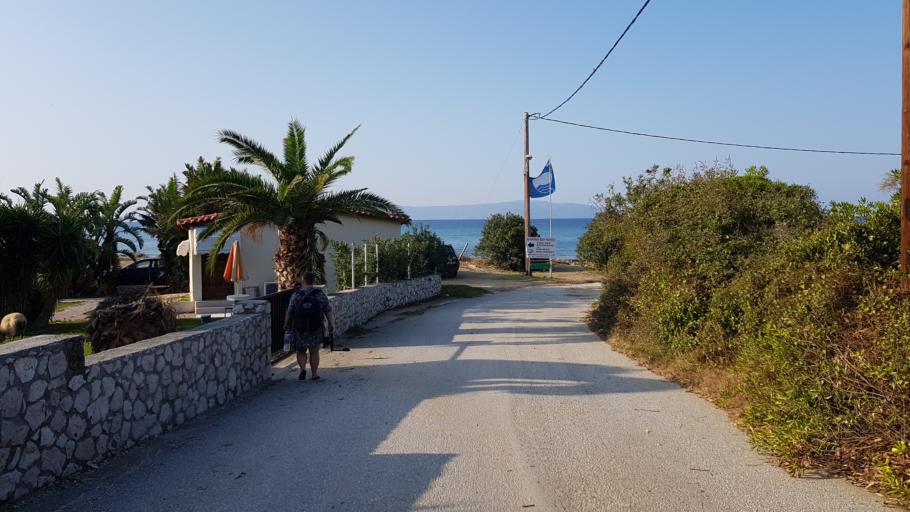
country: GR
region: Ionian Islands
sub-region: Nomos Kefallinias
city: Poros
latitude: 38.0653
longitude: 20.7785
